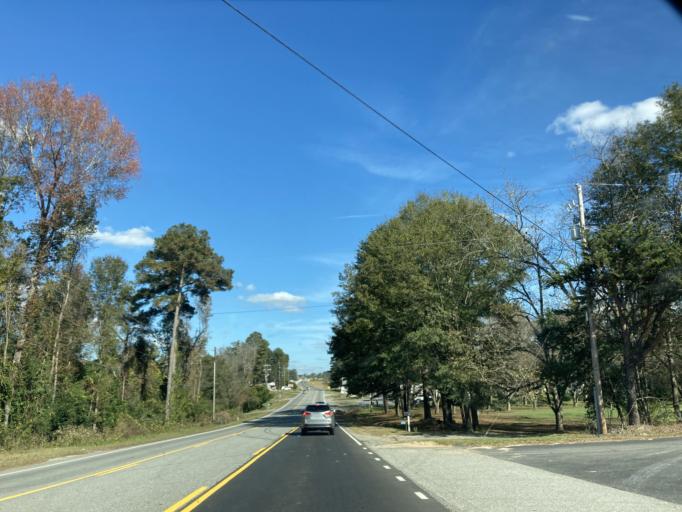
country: US
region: Georgia
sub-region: Bibb County
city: Macon
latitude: 32.8801
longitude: -83.5478
